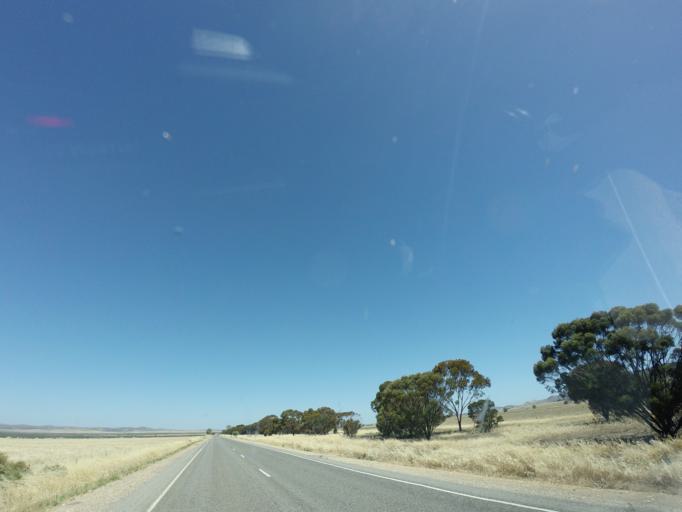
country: AU
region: South Australia
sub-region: Peterborough
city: Peterborough
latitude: -32.7543
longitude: 138.6443
